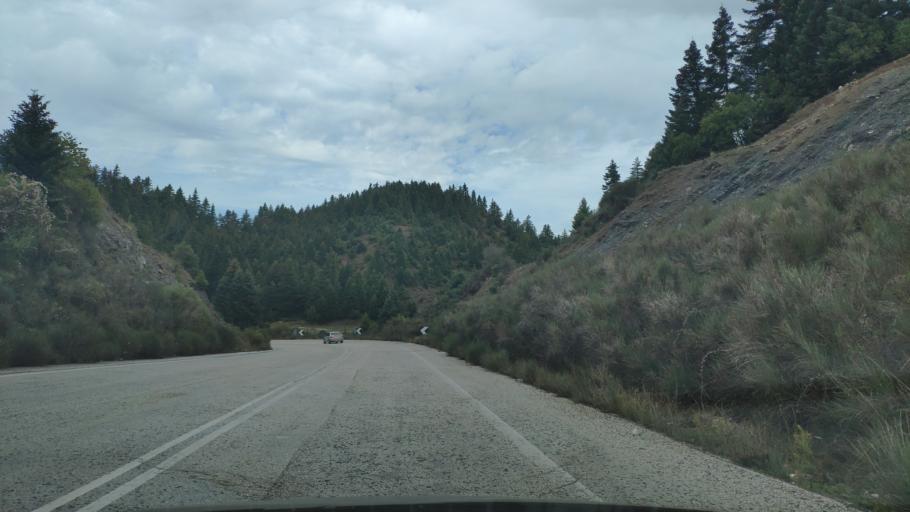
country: GR
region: Peloponnese
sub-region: Nomos Arkadias
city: Dimitsana
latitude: 37.6390
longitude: 22.0933
